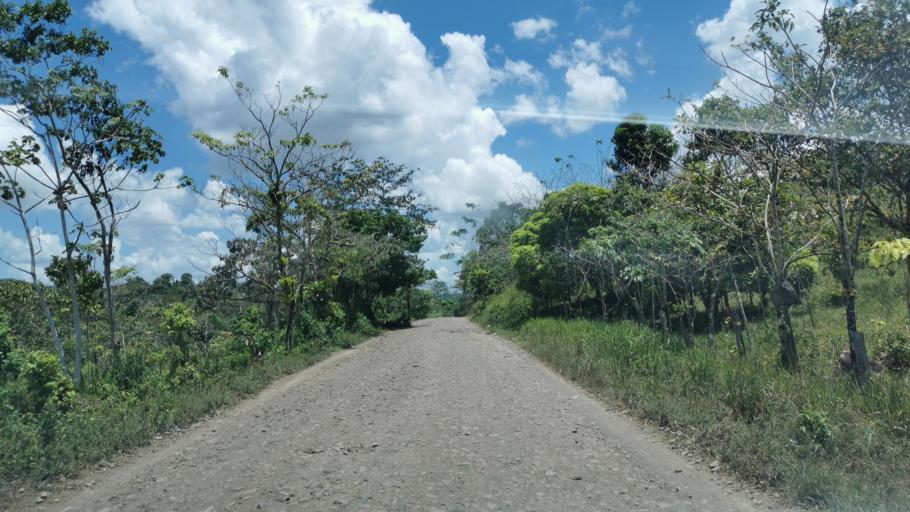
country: NI
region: Atlantico Sur
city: Rama
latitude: 12.3940
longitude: -84.3056
